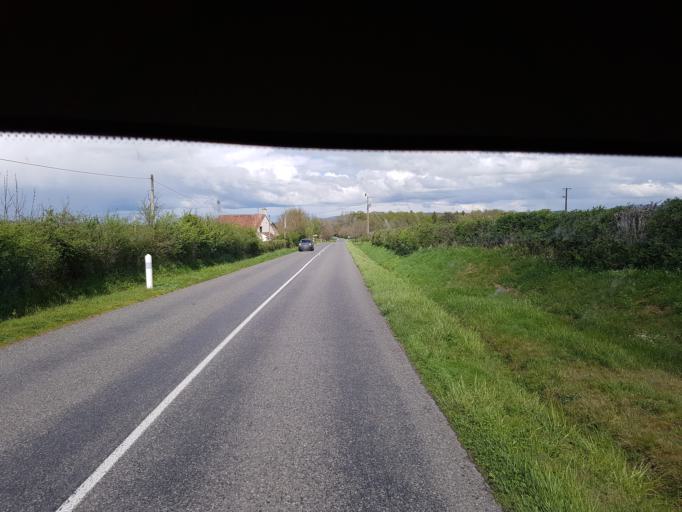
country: FR
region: Bourgogne
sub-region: Departement de Saone-et-Loire
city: Etang-sur-Arroux
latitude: 46.8030
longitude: 4.1524
